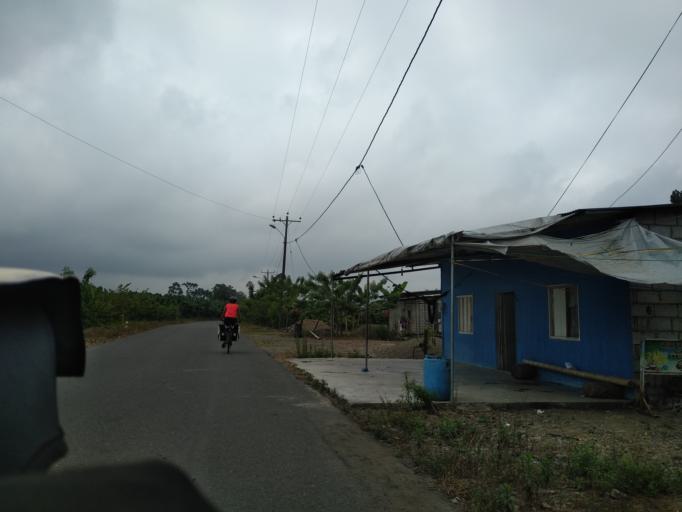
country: EC
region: Los Rios
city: Quevedo
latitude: -0.9750
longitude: -79.3550
